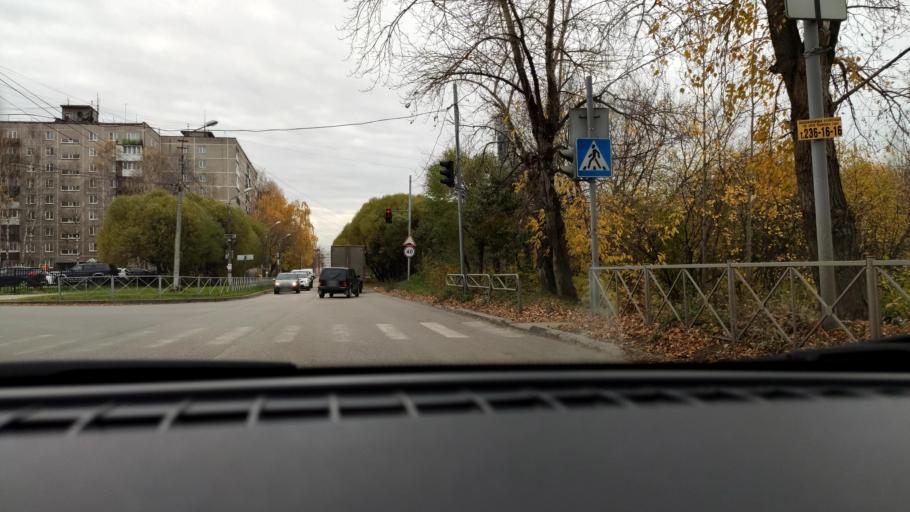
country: RU
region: Perm
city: Perm
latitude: 58.0642
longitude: 56.3540
